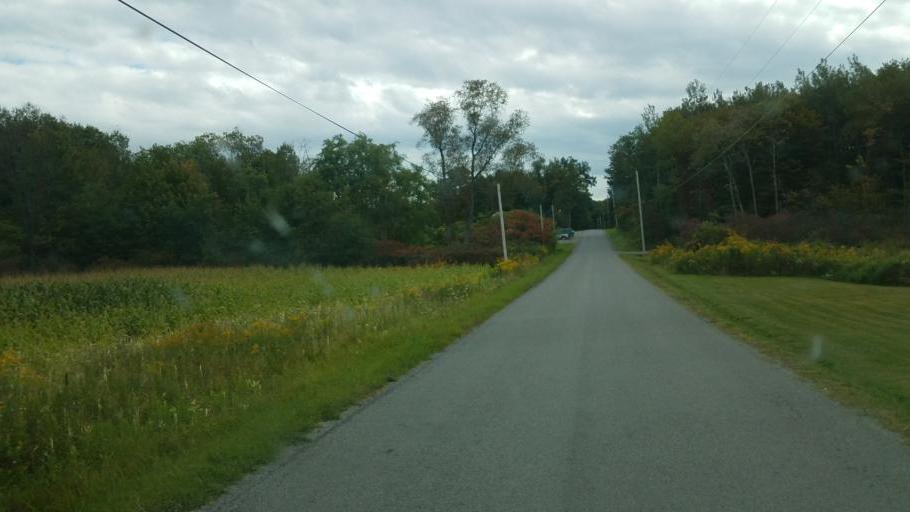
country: US
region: Pennsylvania
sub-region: Crawford County
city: Pymatuning Central
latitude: 41.4874
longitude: -80.4522
